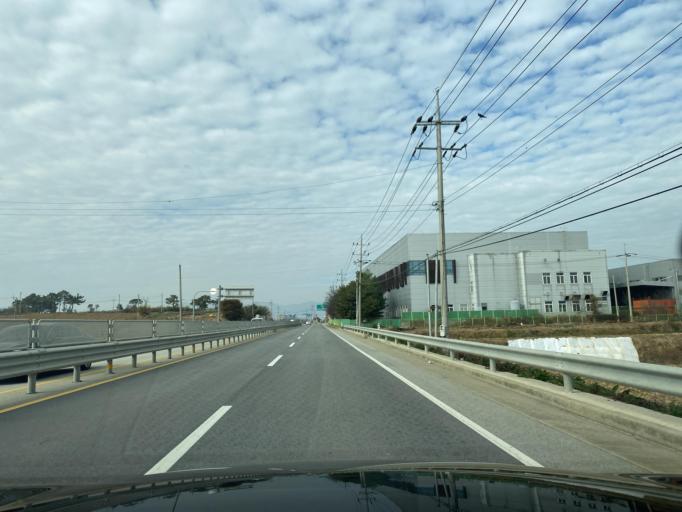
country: KR
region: Chungcheongnam-do
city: Yesan
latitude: 36.6887
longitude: 126.7543
